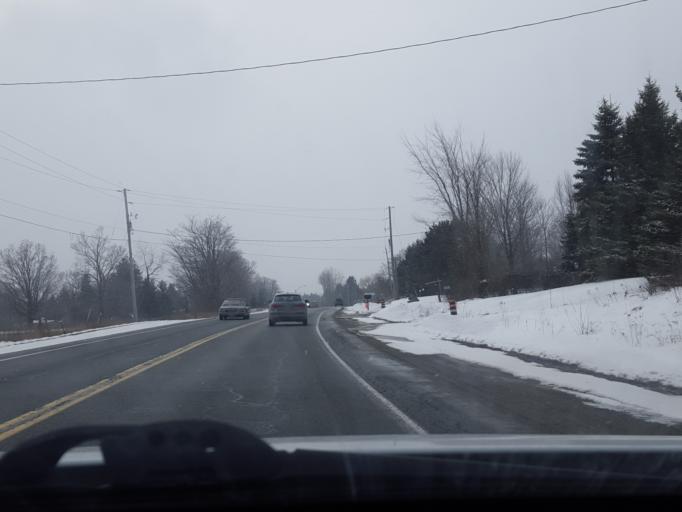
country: CA
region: Ontario
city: Markham
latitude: 44.0072
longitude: -79.2593
